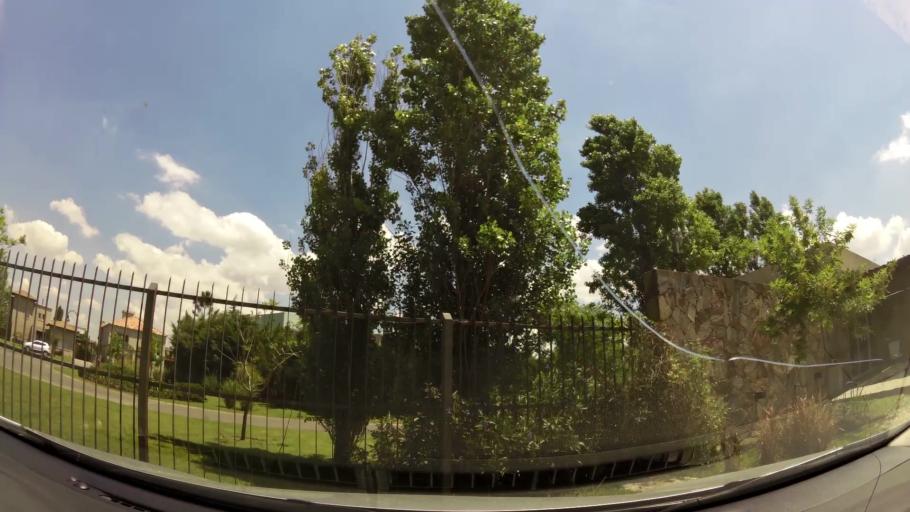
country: AR
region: Buenos Aires
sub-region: Partido de Tigre
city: Tigre
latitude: -34.4253
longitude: -58.6044
